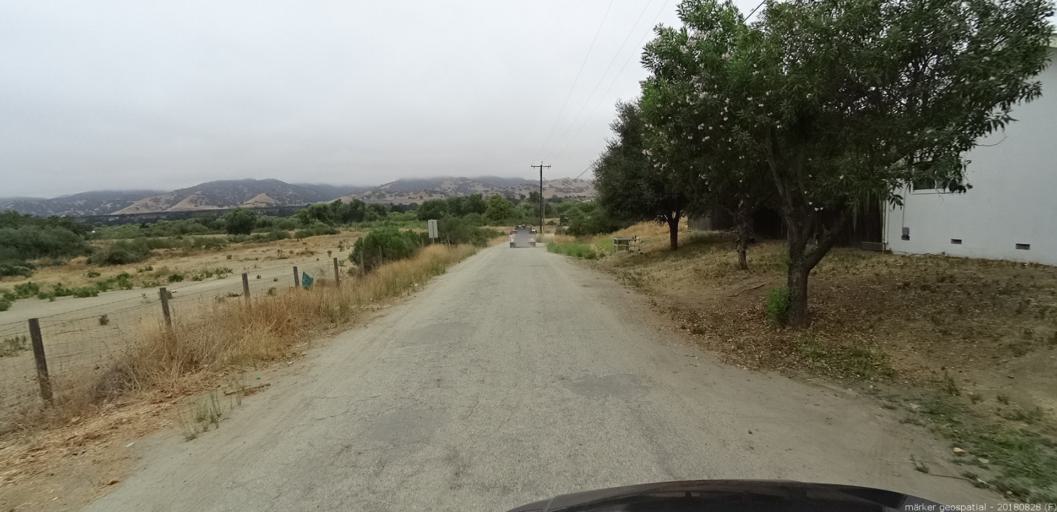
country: US
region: California
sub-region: San Luis Obispo County
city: Lake Nacimiento
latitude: 36.0172
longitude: -120.9077
